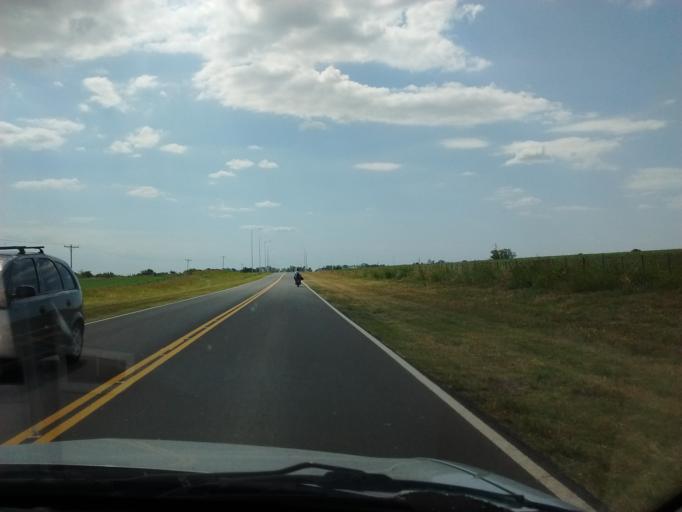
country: AR
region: Entre Rios
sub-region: Departamento de Victoria
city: Victoria
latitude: -32.6623
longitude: -60.0500
